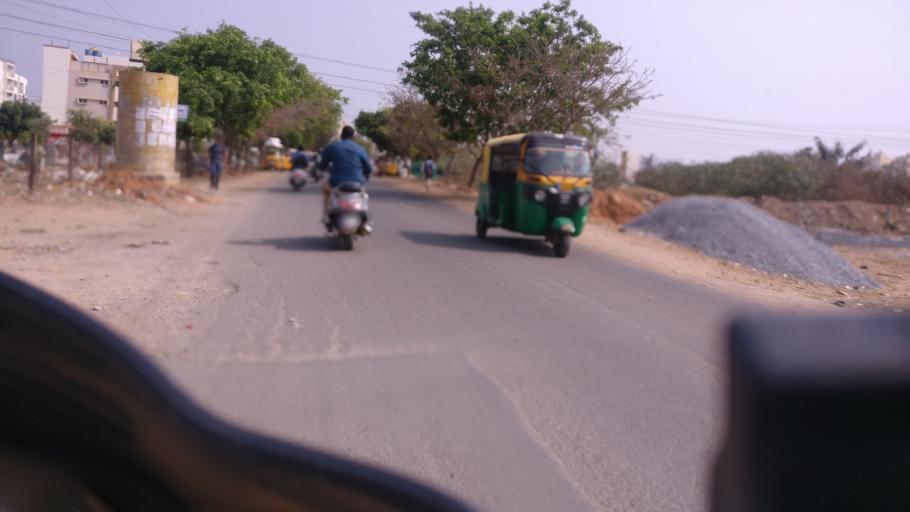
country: IN
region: Karnataka
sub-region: Bangalore Urban
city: Bangalore
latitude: 12.8746
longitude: 77.6543
